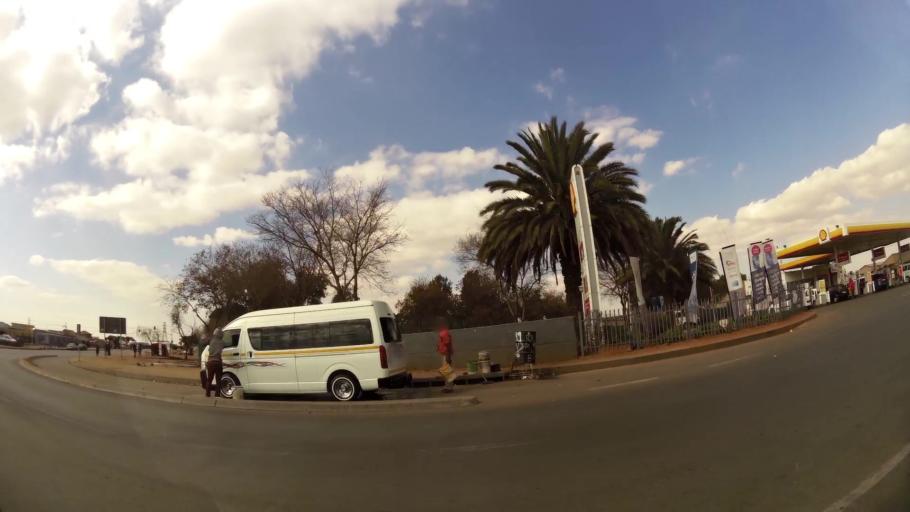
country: ZA
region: Gauteng
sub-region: Ekurhuleni Metropolitan Municipality
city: Tembisa
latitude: -25.9986
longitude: 28.2418
